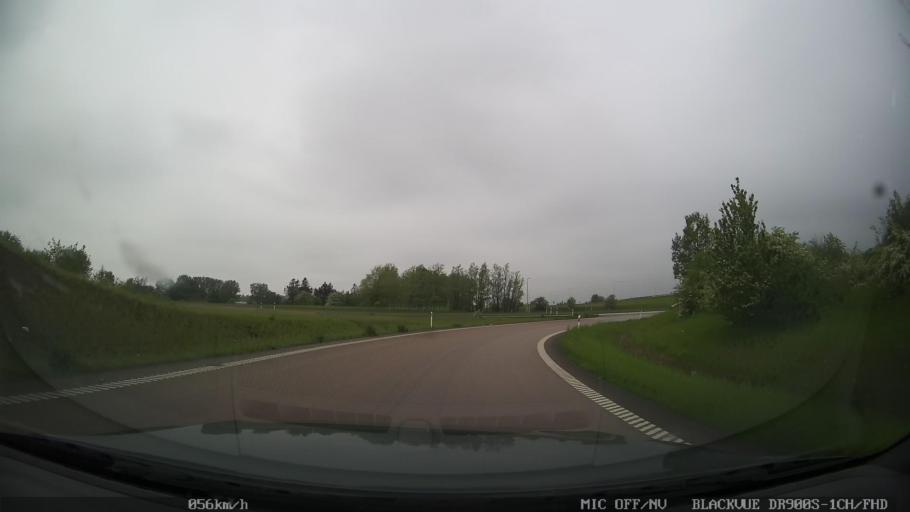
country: SE
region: Skane
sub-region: Landskrona
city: Landskrona
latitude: 55.8739
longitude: 12.8804
